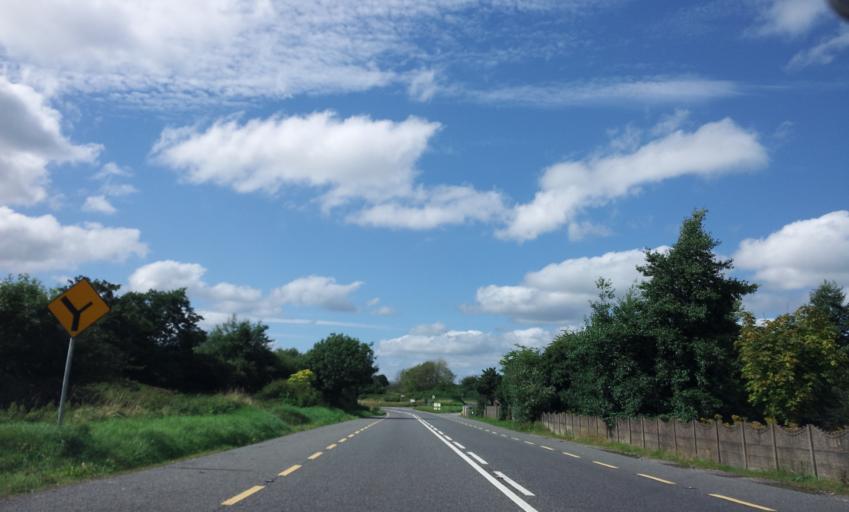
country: IE
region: Munster
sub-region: County Cork
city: Macroom
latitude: 51.8661
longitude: -8.8939
